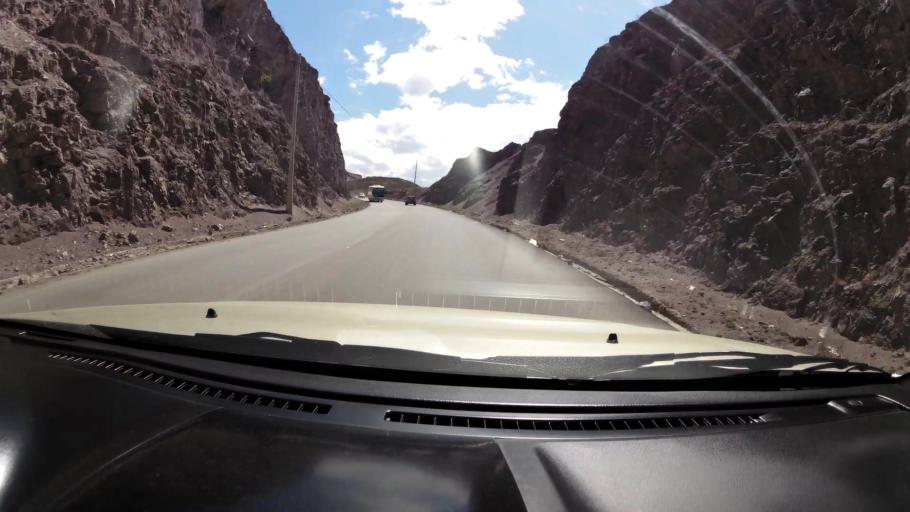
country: EC
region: El Oro
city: Zaruma
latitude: -3.3258
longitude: -79.3589
